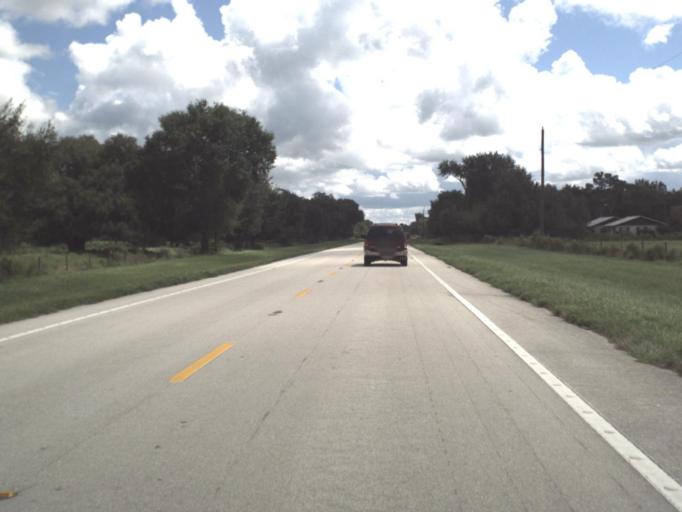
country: US
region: Florida
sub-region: DeSoto County
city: Arcadia
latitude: 27.2737
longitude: -82.0121
